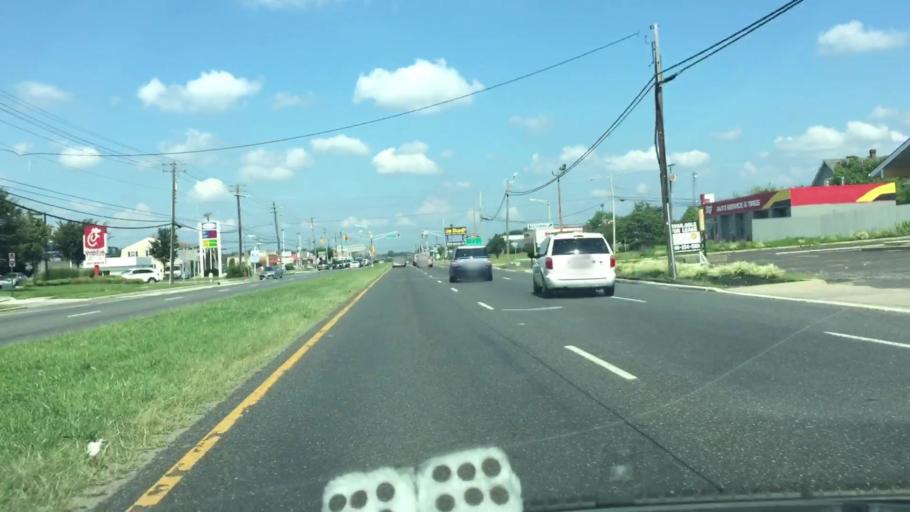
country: US
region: New Jersey
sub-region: Gloucester County
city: Turnersville
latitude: 39.7584
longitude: -75.0472
